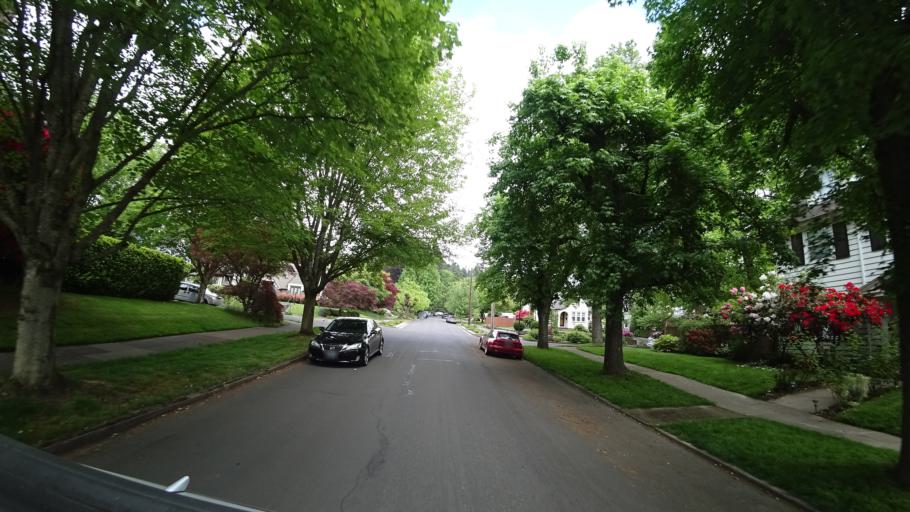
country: US
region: Oregon
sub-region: Multnomah County
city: Lents
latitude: 45.5129
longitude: -122.6041
